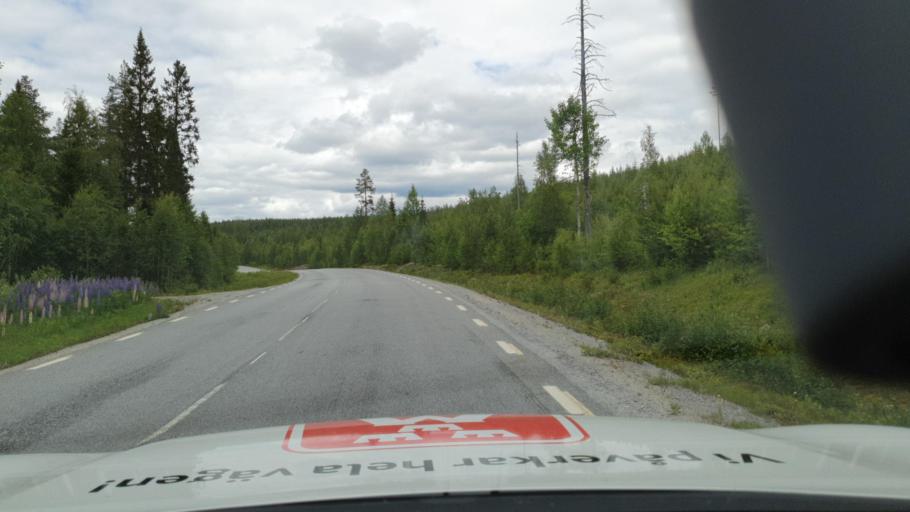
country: SE
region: Vaesterbotten
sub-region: Bjurholms Kommun
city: Bjurholm
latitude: 63.8796
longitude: 19.0177
